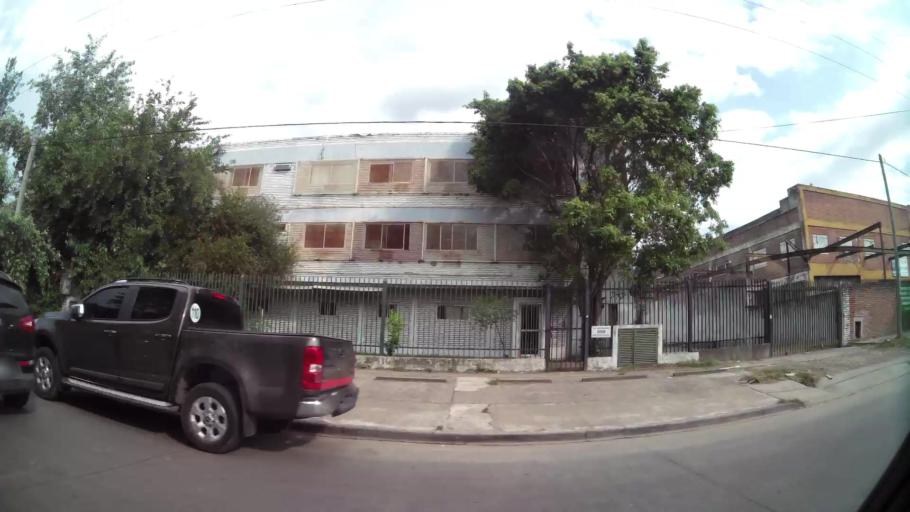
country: AR
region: Buenos Aires
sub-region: Partido de Tigre
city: Tigre
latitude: -34.4781
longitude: -58.6283
